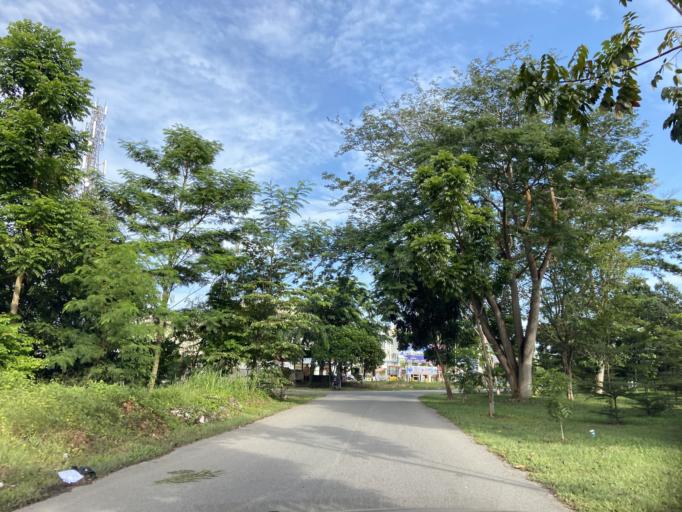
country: SG
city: Singapore
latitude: 1.1061
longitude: 104.0313
